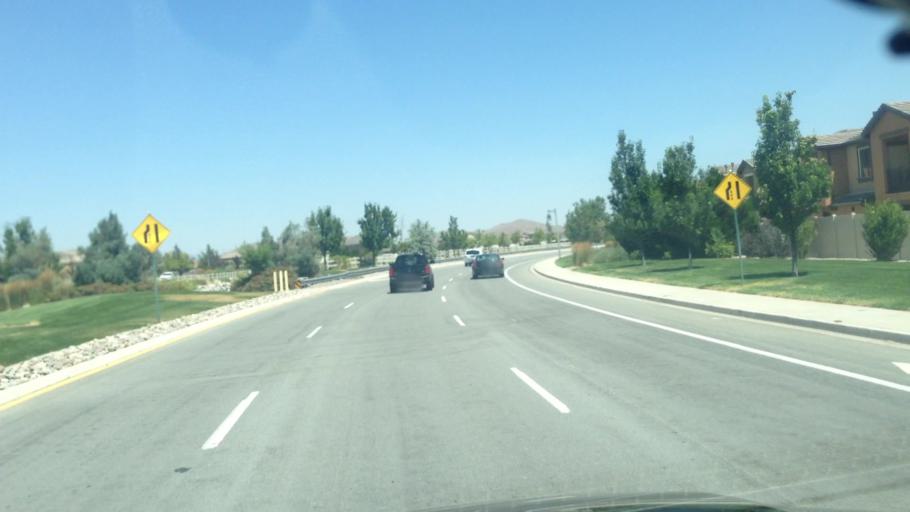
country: US
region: Nevada
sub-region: Washoe County
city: Sparks
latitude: 39.4236
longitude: -119.7331
